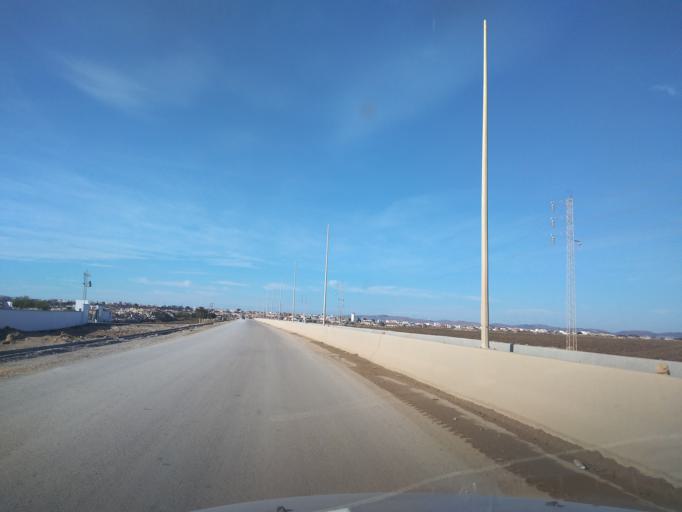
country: TN
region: Ariana
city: Qal'at al Andalus
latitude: 37.0399
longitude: 10.1315
